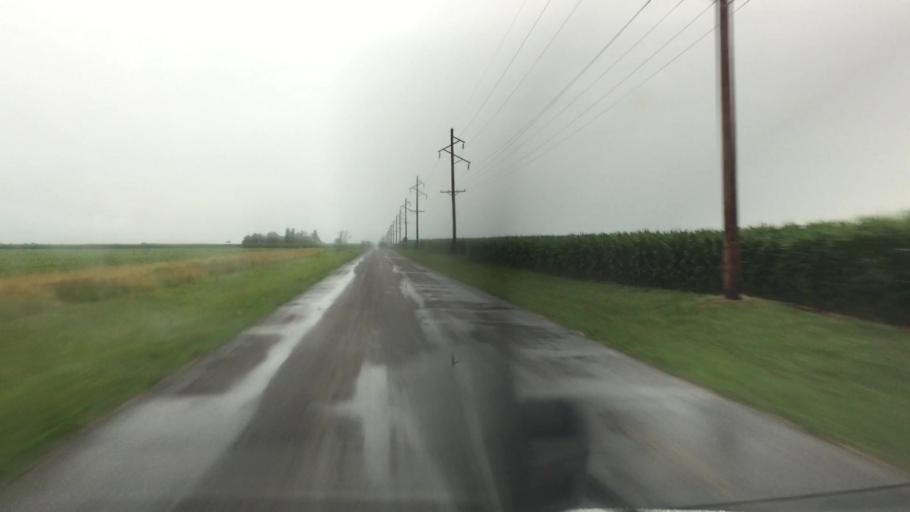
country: US
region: Illinois
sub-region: Hancock County
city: Nauvoo
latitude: 40.5153
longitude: -91.2693
